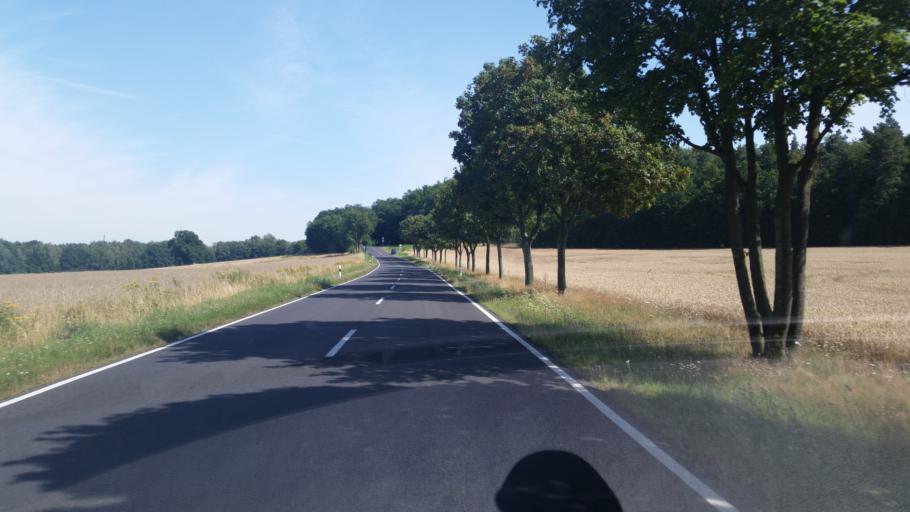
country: DE
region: Saxony
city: Kamenz
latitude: 51.2838
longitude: 14.0648
